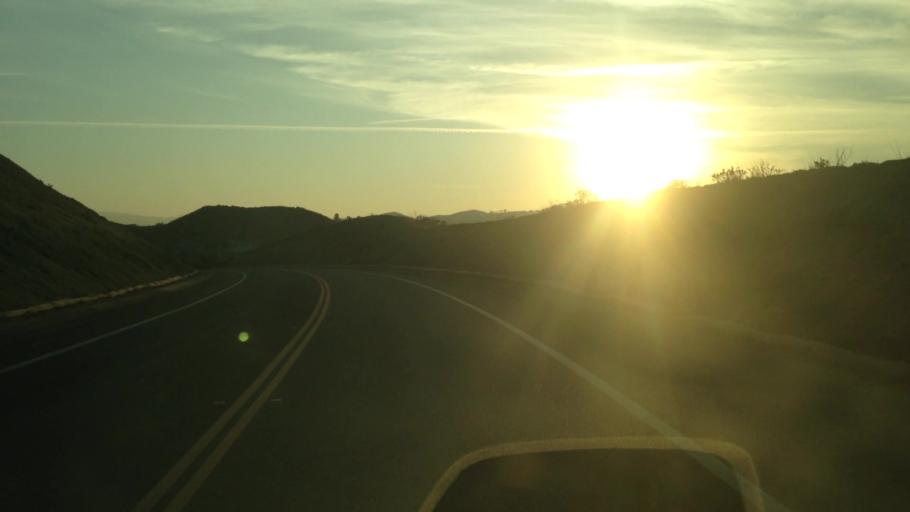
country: US
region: California
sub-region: Riverside County
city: Riverside
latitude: 33.8891
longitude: -117.4297
